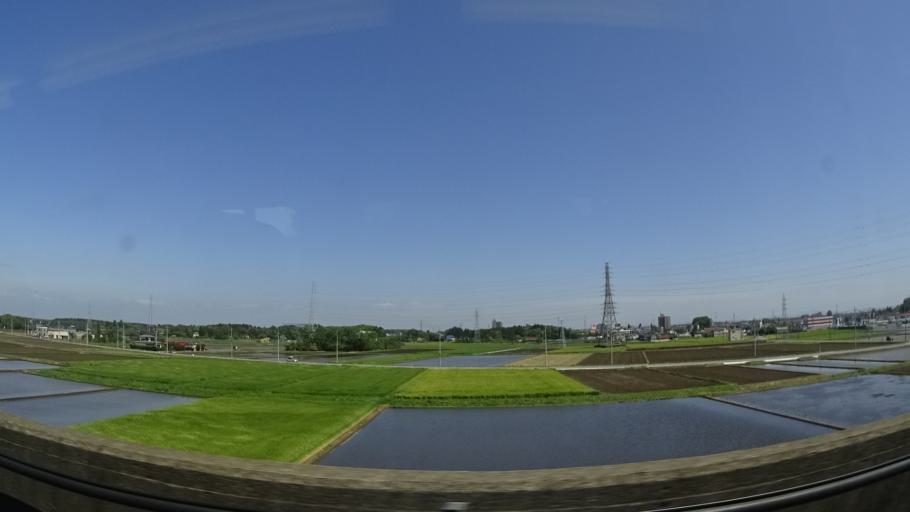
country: JP
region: Tochigi
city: Utsunomiya-shi
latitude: 36.5963
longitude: 139.9055
